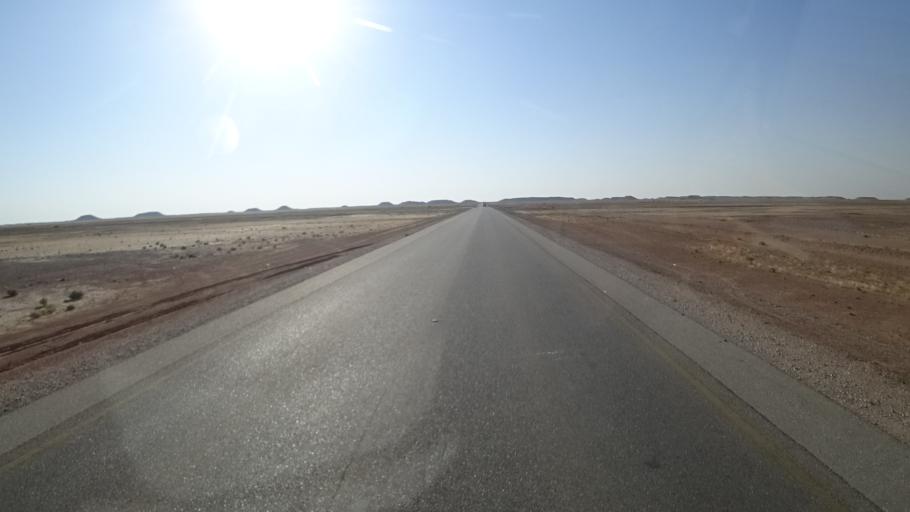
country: OM
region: Zufar
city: Salalah
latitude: 17.6419
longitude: 53.8295
